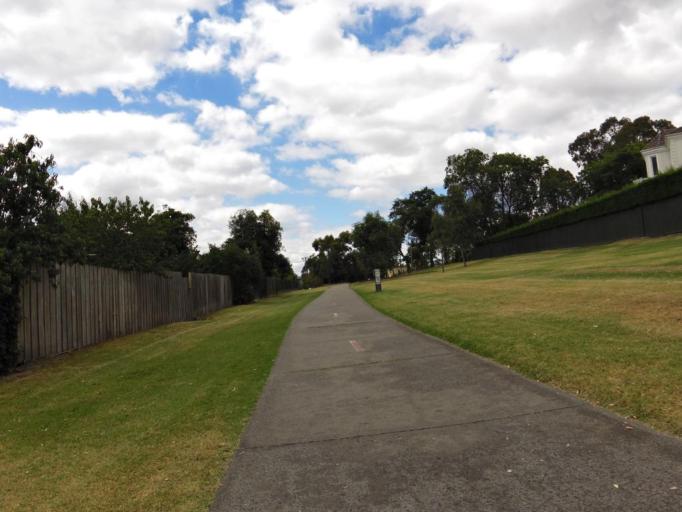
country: AU
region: Victoria
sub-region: Boroondara
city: Kew East
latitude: -37.8054
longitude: 145.0606
